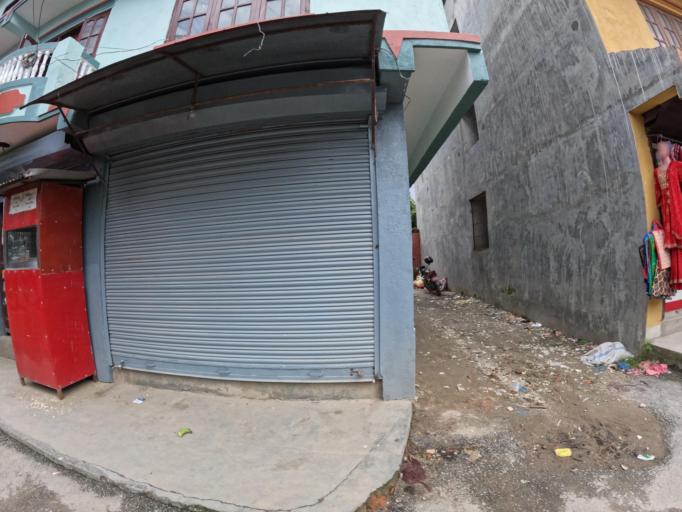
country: NP
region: Central Region
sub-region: Bagmati Zone
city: Kathmandu
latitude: 27.7495
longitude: 85.3160
